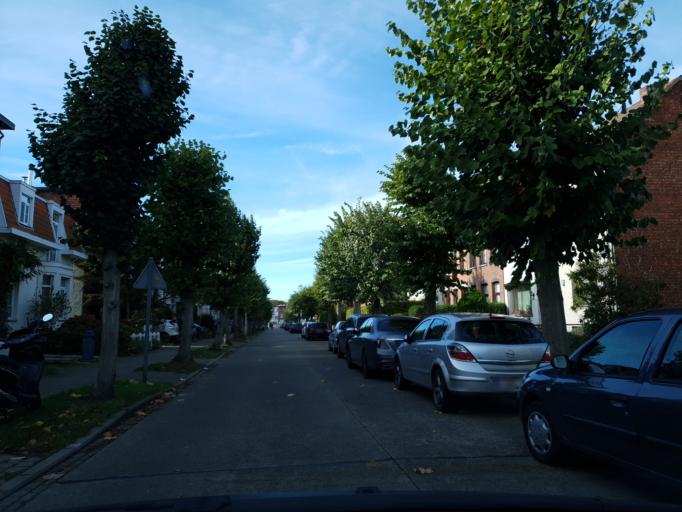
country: BE
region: Flanders
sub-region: Provincie Antwerpen
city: Schoten
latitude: 51.2460
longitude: 4.4634
